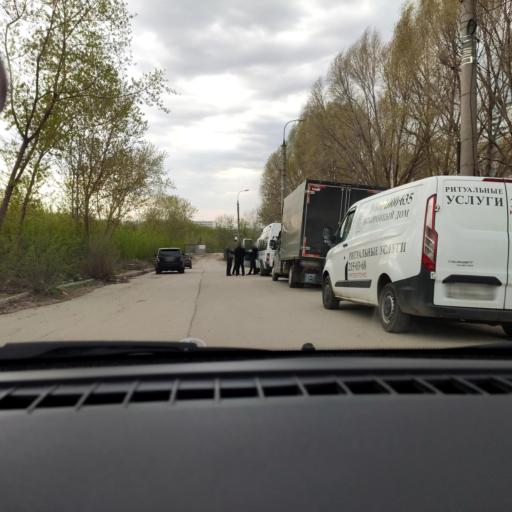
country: RU
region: Samara
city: Samara
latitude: 53.1898
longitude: 50.1528
